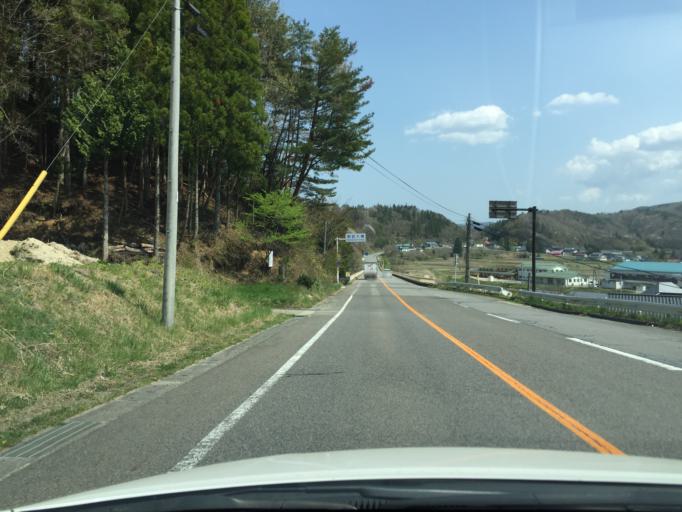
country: JP
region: Fukushima
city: Namie
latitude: 37.4409
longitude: 140.7919
